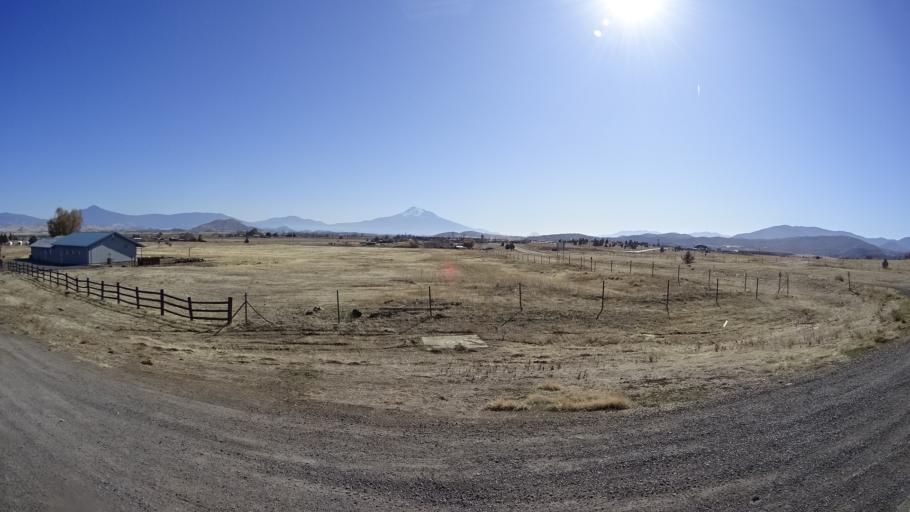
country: US
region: California
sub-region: Siskiyou County
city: Yreka
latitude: 41.7409
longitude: -122.5990
